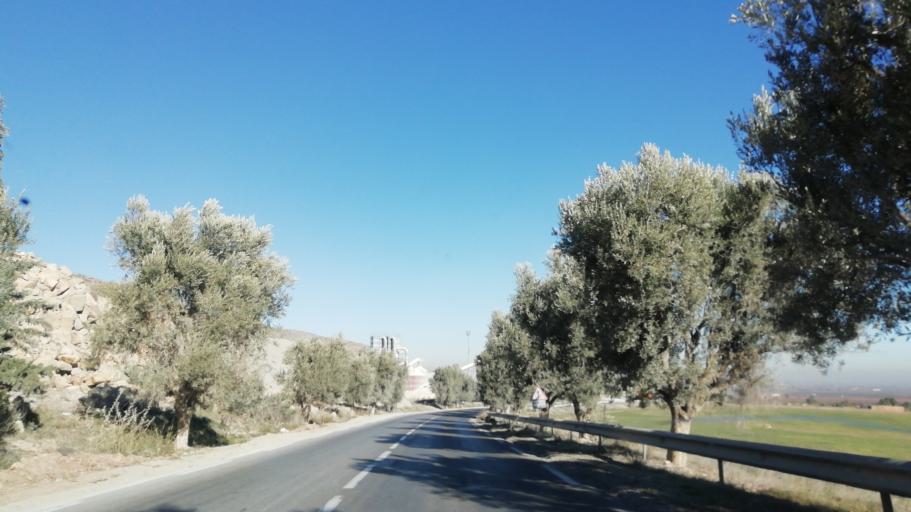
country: DZ
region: Mascara
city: Mascara
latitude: 35.2506
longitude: 0.1218
